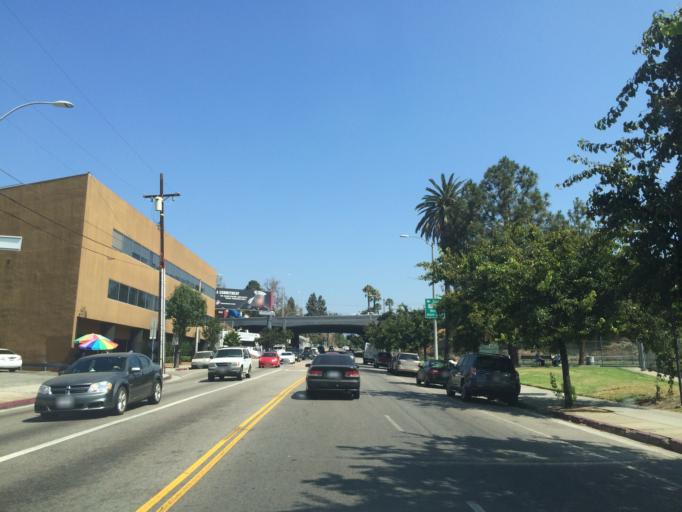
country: US
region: California
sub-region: Los Angeles County
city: Echo Park
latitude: 34.0682
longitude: -118.2609
